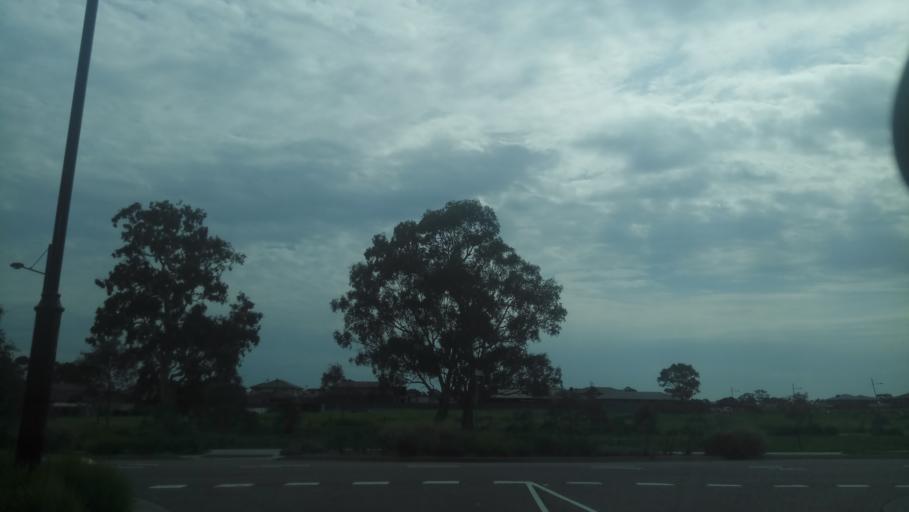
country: AU
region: Victoria
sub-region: Greater Dandenong
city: Keysborough
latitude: -38.0091
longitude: 145.1675
